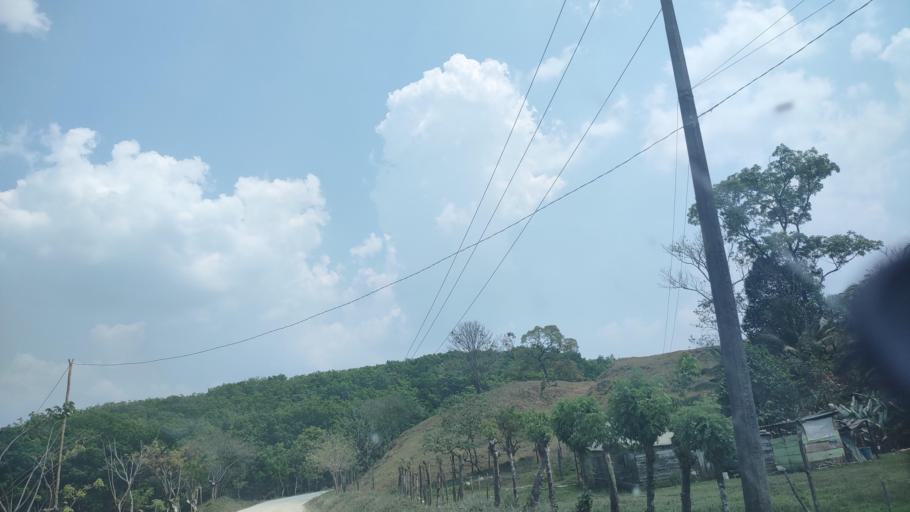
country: MX
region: Tabasco
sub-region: Huimanguillo
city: Francisco Rueda
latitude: 17.6059
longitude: -93.9062
